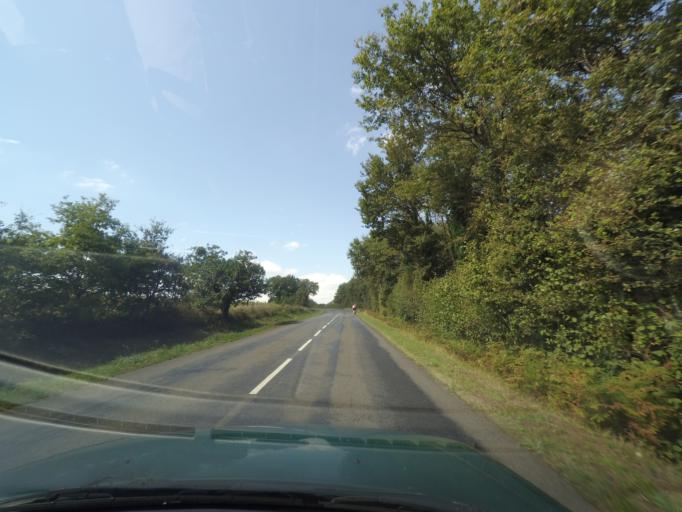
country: FR
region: Pays de la Loire
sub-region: Departement de la Loire-Atlantique
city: Saint-Lumine-de-Coutais
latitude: 47.0560
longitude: -1.7499
